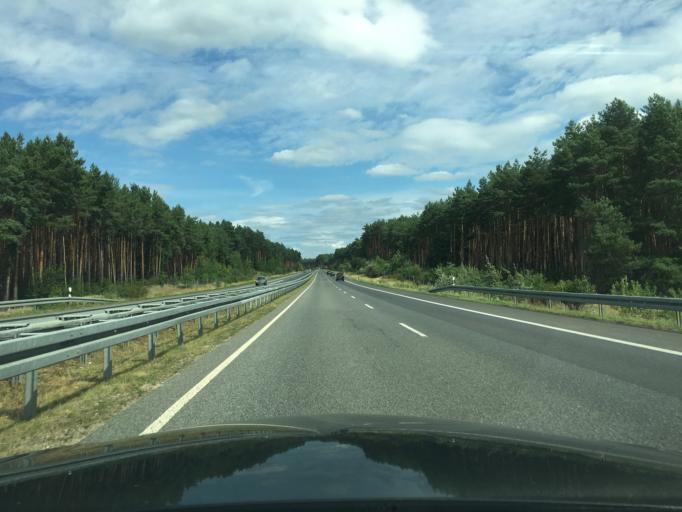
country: DE
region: Brandenburg
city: Oranienburg
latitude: 52.7782
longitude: 13.2220
